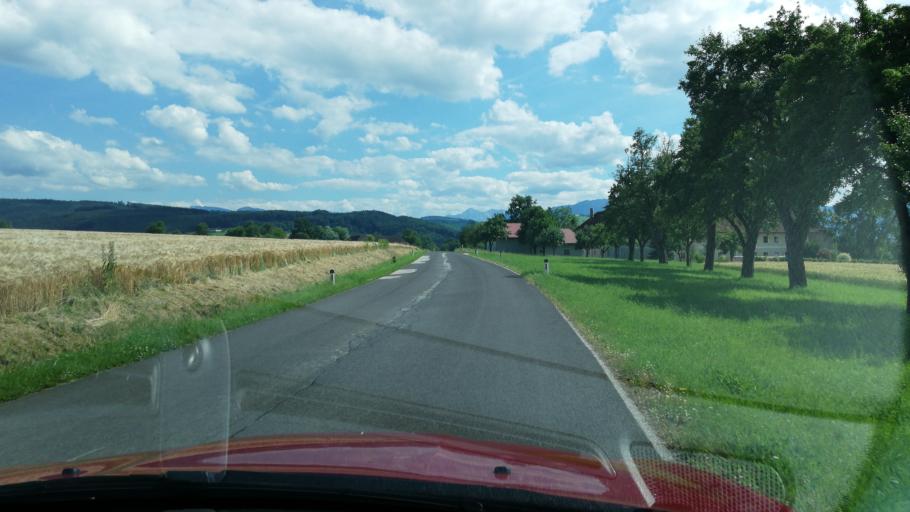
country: AT
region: Upper Austria
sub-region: Politischer Bezirk Steyr-Land
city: Pfarrkirchen bei Bad Hall
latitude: 47.9868
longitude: 14.1597
